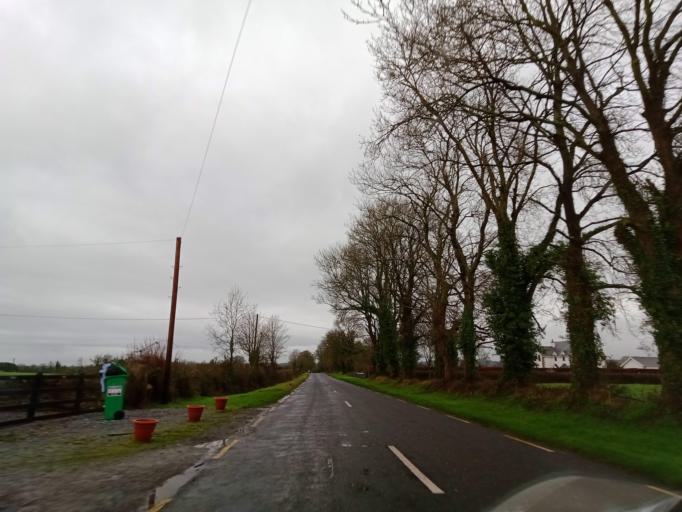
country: IE
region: Leinster
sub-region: Kilkenny
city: Callan
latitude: 52.5697
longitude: -7.4471
